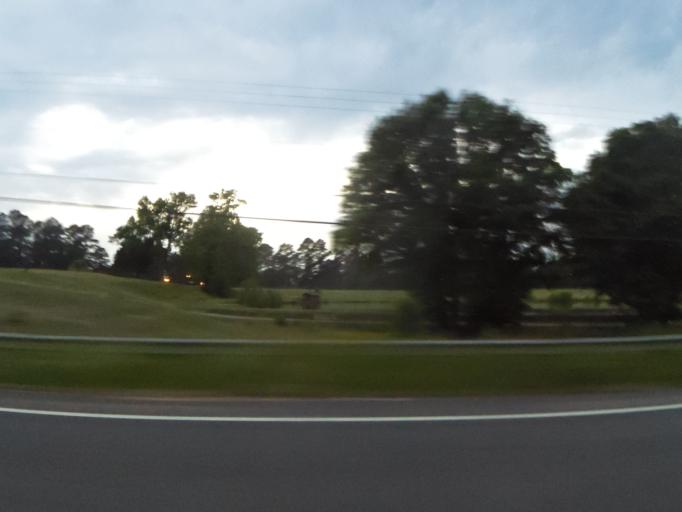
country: US
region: Georgia
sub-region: McDuffie County
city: Thomson
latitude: 33.5361
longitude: -82.5072
